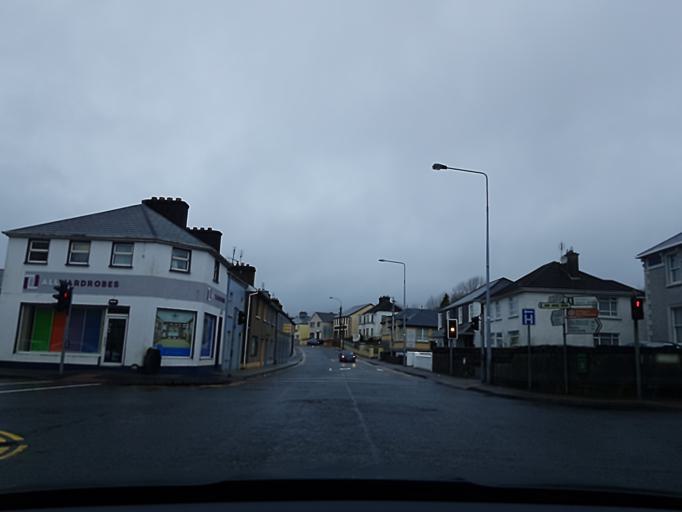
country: IE
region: Connaught
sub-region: Maigh Eo
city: Castlebar
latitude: 53.8573
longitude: -9.3021
